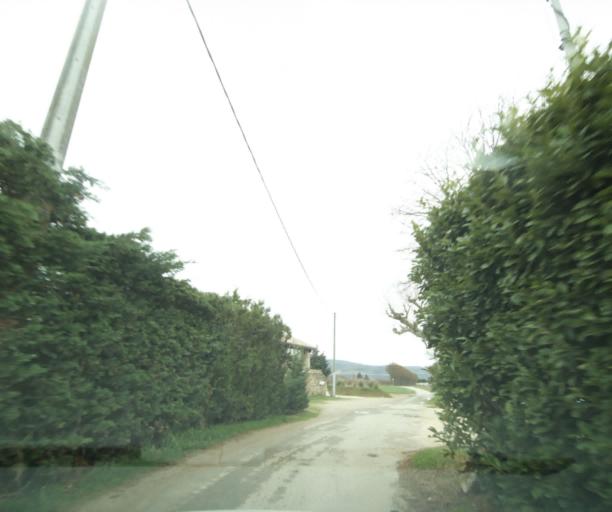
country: FR
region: Rhone-Alpes
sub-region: Departement de la Drome
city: Bourg-les-Valence
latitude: 44.9705
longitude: 4.9073
